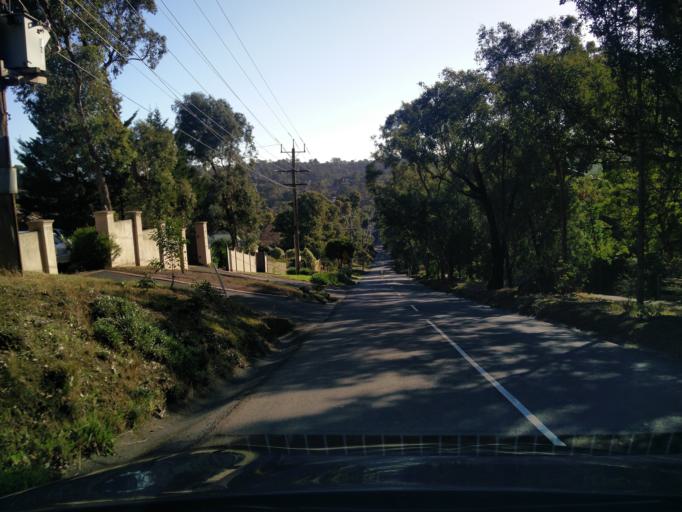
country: AU
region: Victoria
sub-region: Nillumbik
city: Research
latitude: -37.7080
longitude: 145.1754
